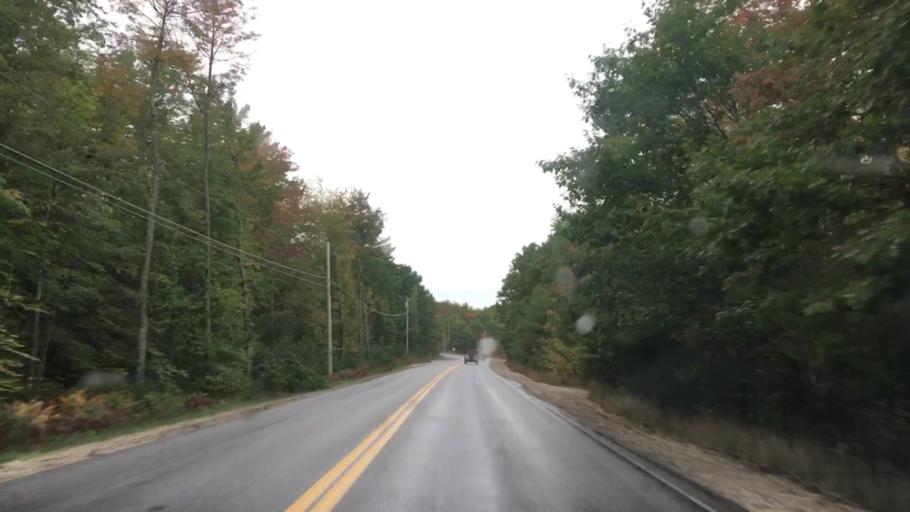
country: US
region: Maine
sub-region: Cumberland County
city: Raymond
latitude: 43.9281
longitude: -70.3786
